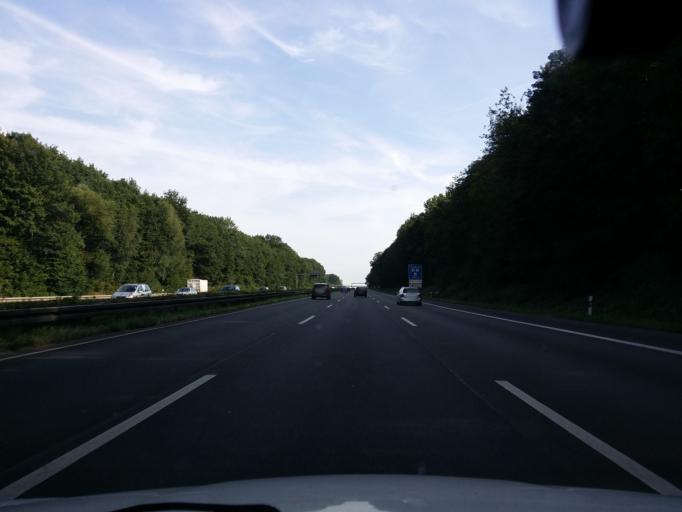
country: DE
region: North Rhine-Westphalia
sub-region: Regierungsbezirk Koln
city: Siegburg
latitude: 50.8146
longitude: 7.2131
